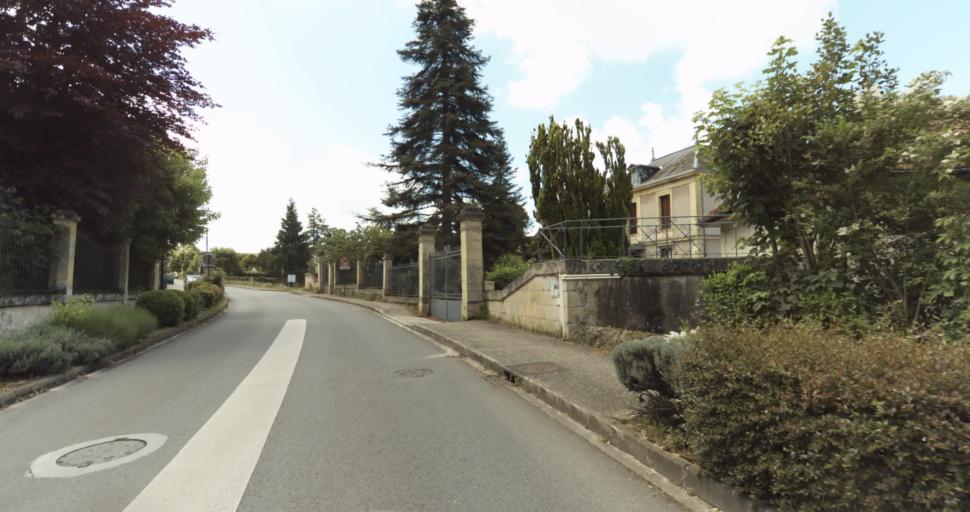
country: FR
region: Aquitaine
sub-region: Departement de la Dordogne
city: Lalinde
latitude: 44.8242
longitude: 0.7061
